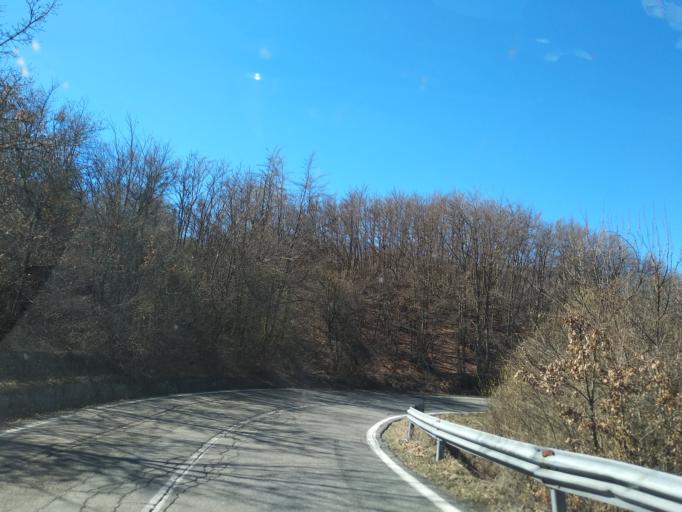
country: IT
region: Emilia-Romagna
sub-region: Provincia di Reggio Emilia
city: Busana
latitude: 44.4060
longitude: 10.3273
